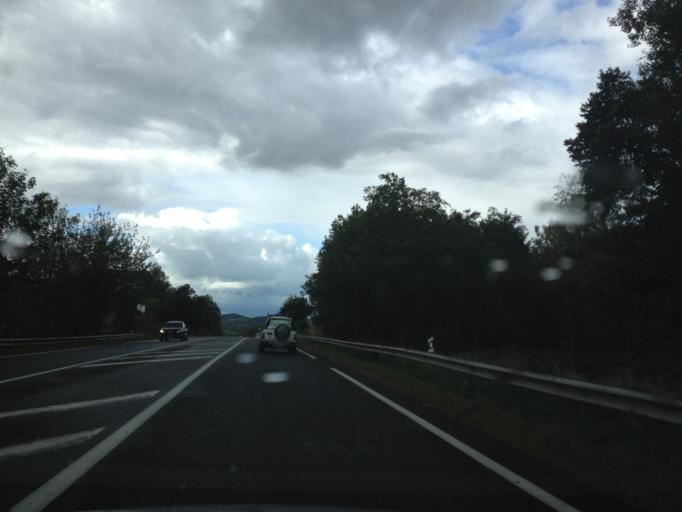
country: FR
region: Rhone-Alpes
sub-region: Departement de la Loire
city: Saint-Symphorien-de-Lay
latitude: 45.9504
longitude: 4.2017
